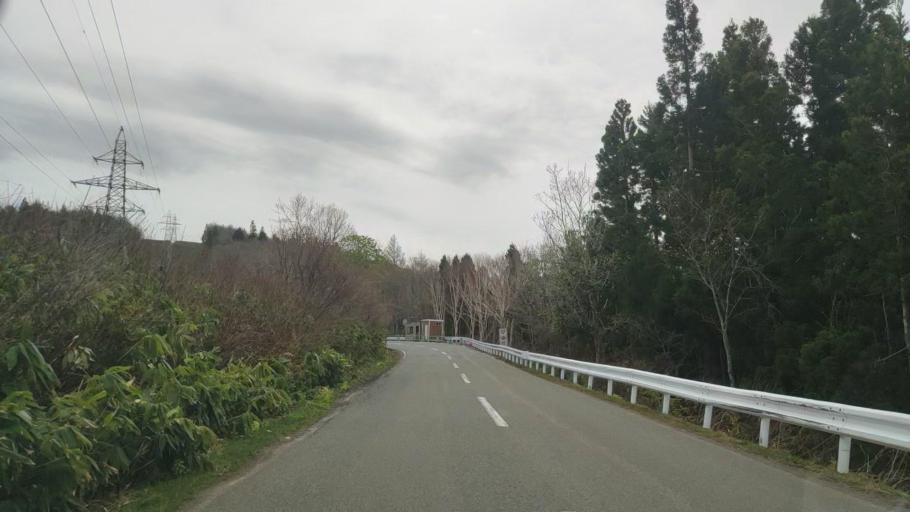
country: JP
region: Aomori
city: Aomori Shi
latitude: 40.7180
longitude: 140.8660
